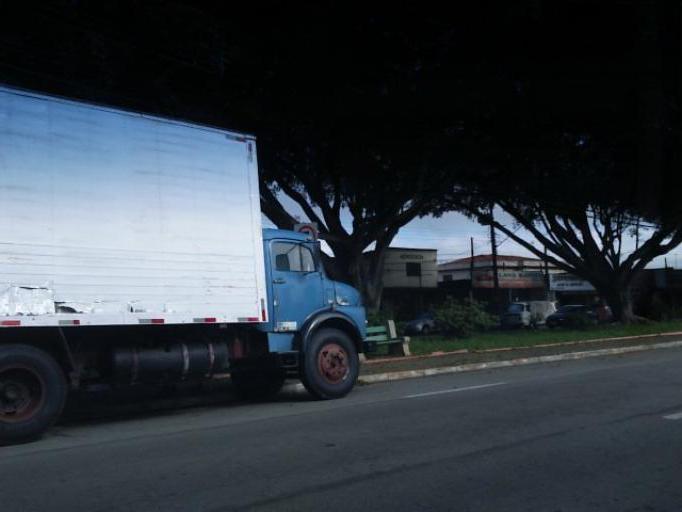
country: BR
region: Sao Paulo
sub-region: Sao Jose Dos Campos
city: Sao Jose dos Campos
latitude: -23.1913
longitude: -45.8748
